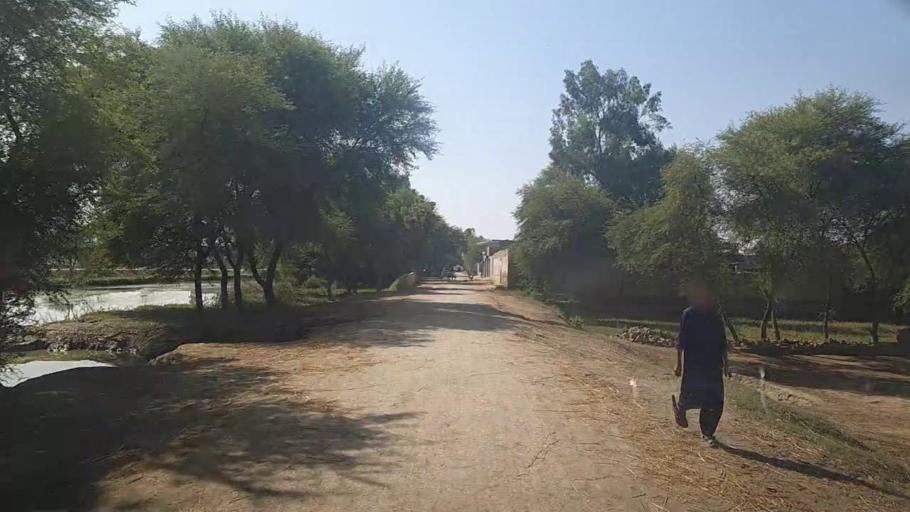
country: PK
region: Sindh
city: Thul
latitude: 28.2391
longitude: 68.7926
